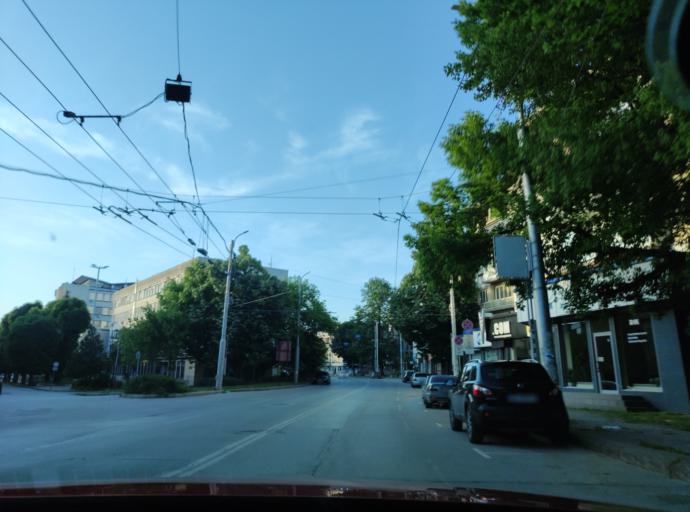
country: BG
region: Pleven
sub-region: Obshtina Pleven
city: Pleven
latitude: 43.4054
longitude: 24.6209
